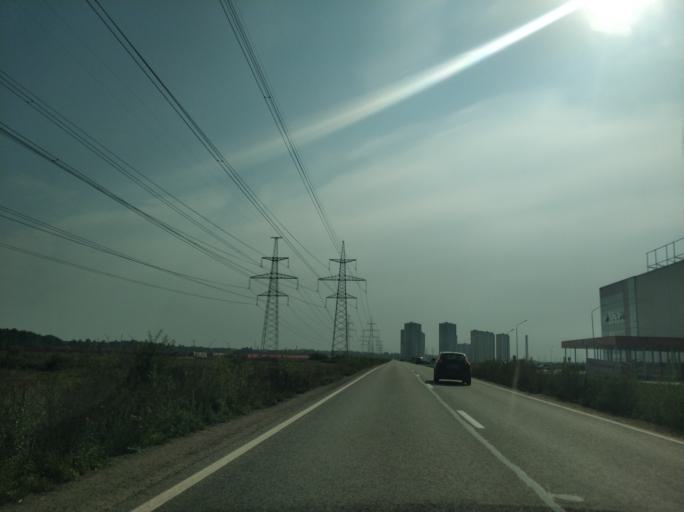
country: RU
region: Leningrad
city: Murino
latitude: 60.0196
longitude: 30.4676
